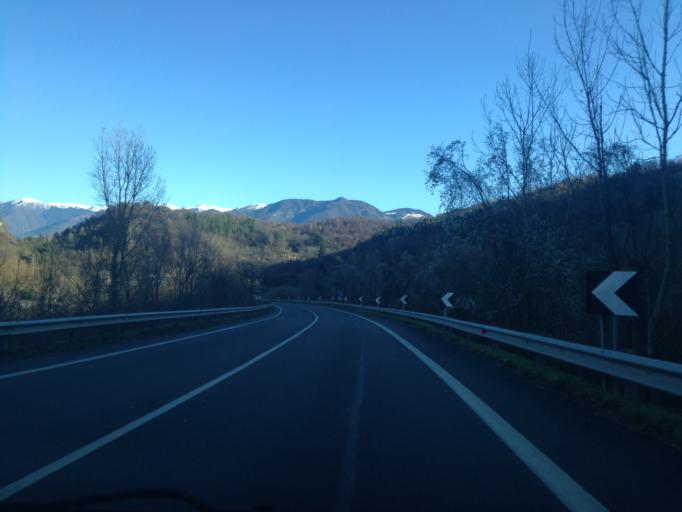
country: IT
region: Lombardy
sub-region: Provincia di Bergamo
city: Pianico
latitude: 45.8050
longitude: 10.0447
